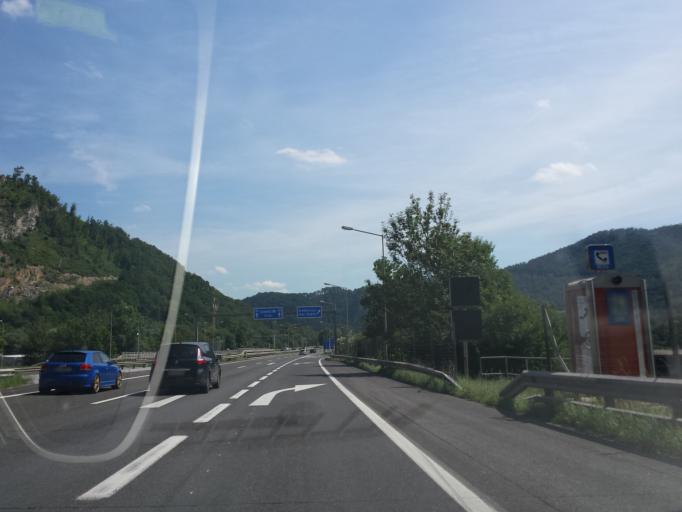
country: AT
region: Styria
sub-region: Politischer Bezirk Graz-Umgebung
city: Gratkorn
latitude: 47.1221
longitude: 15.3684
